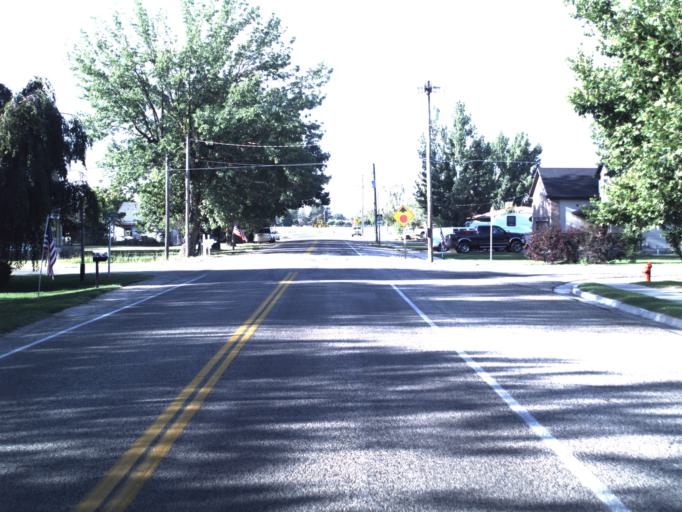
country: US
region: Utah
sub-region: Weber County
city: Plain City
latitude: 41.2997
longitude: -112.0846
